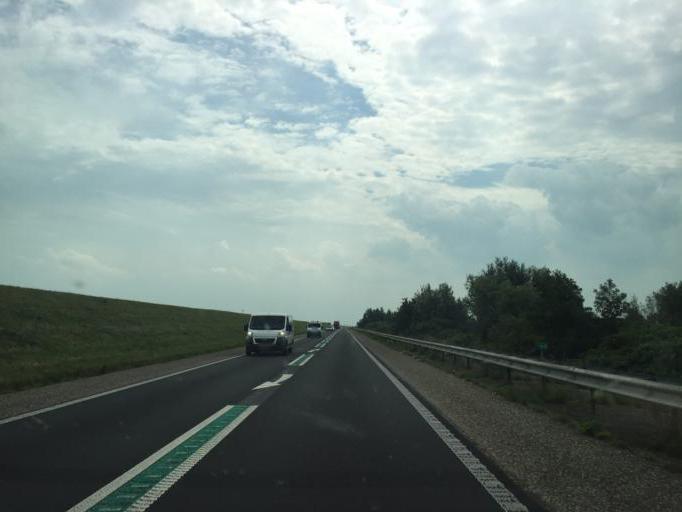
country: NL
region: North Holland
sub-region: Gemeente Enkhuizen
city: Enkhuizen
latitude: 52.6444
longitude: 5.4039
